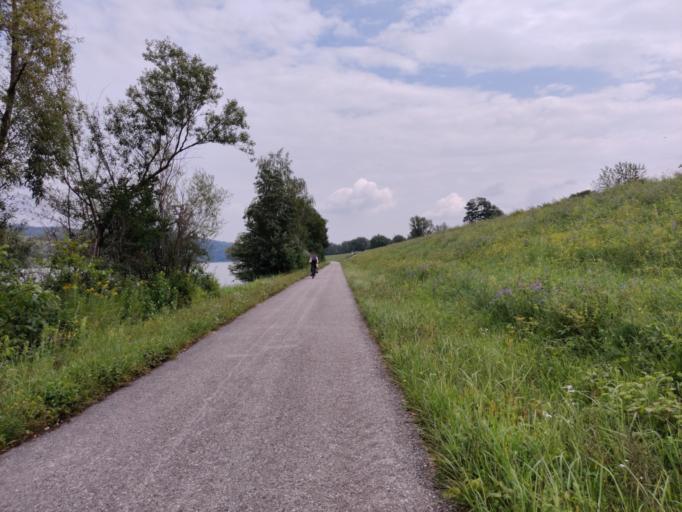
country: AT
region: Lower Austria
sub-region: Politischer Bezirk Melk
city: Marbach an der Donau
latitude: 48.2118
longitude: 15.1612
